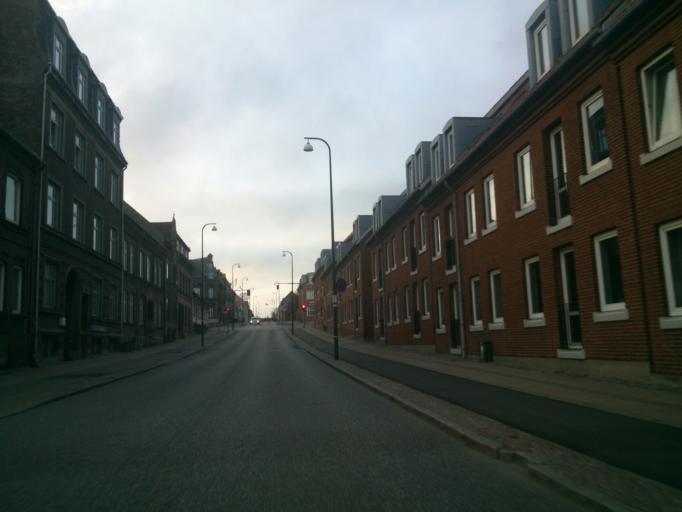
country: DK
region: South Denmark
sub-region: Fredericia Kommune
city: Fredericia
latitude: 55.5631
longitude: 9.7527
